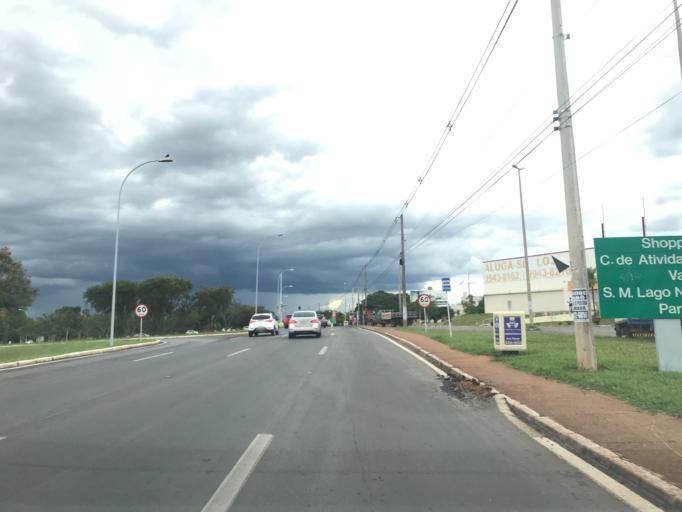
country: BR
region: Federal District
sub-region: Brasilia
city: Brasilia
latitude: -15.7221
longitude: -47.8821
